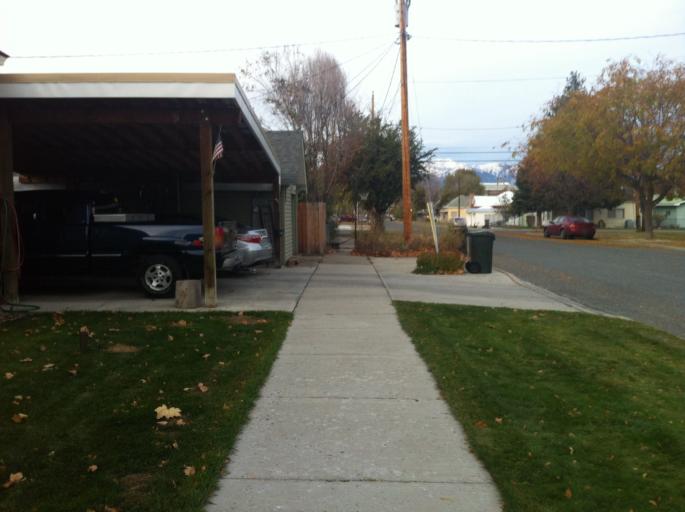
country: US
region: Oregon
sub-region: Baker County
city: Baker City
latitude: 44.7835
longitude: -117.8350
